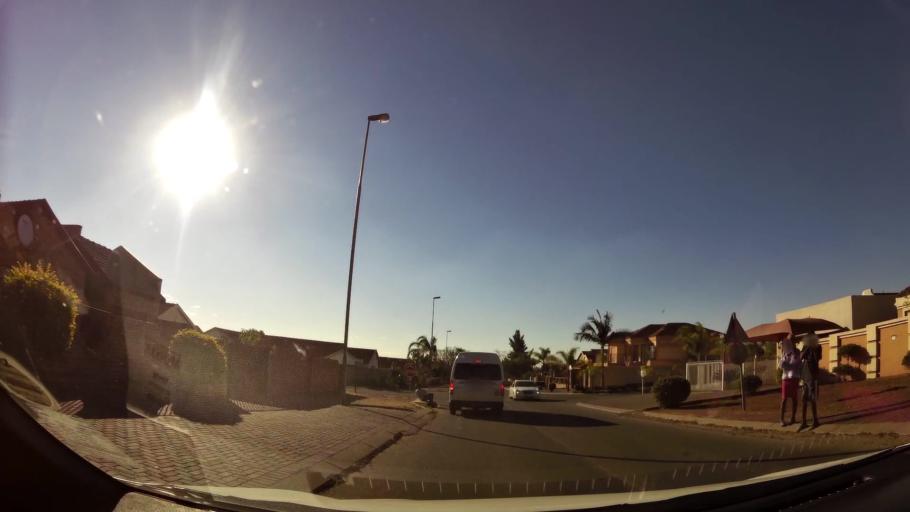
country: ZA
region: Limpopo
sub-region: Capricorn District Municipality
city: Polokwane
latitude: -23.8835
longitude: 29.4742
